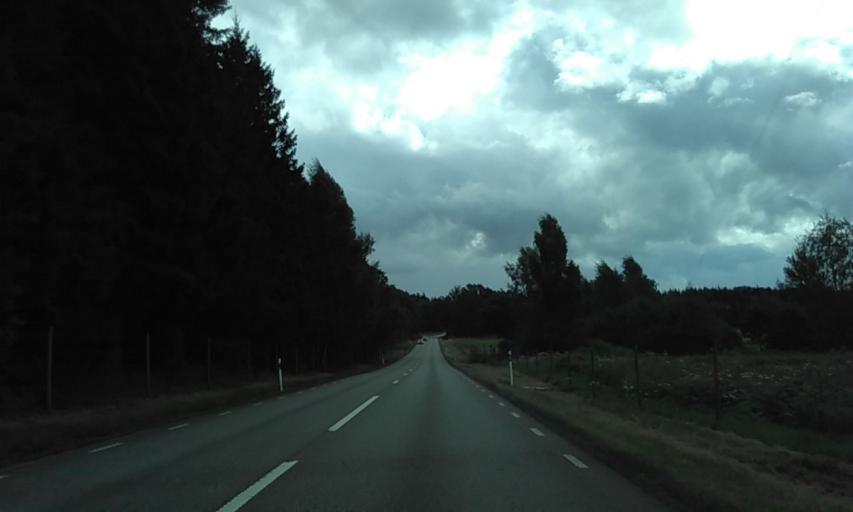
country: SE
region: Vaestra Goetaland
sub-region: Alingsas Kommun
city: Alingsas
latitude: 57.9617
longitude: 12.4461
